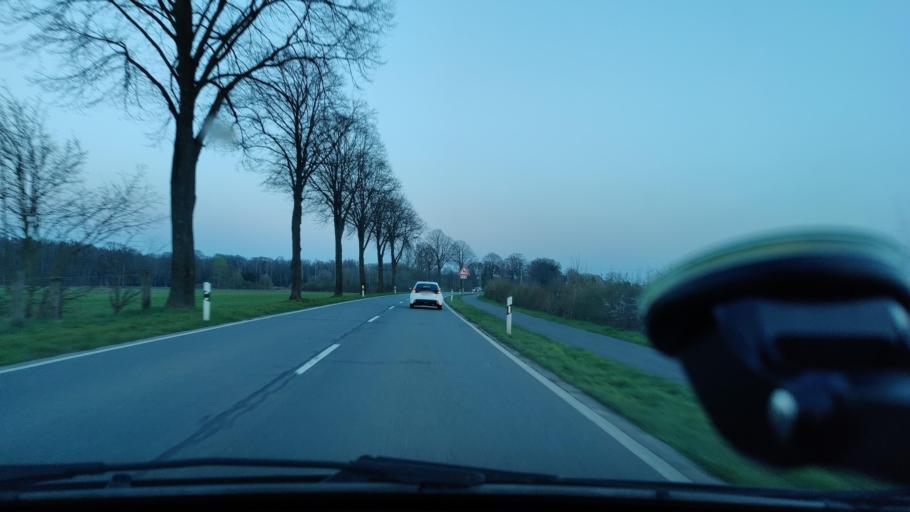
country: DE
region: North Rhine-Westphalia
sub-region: Regierungsbezirk Dusseldorf
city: Kevelaer
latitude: 51.5313
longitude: 6.2578
